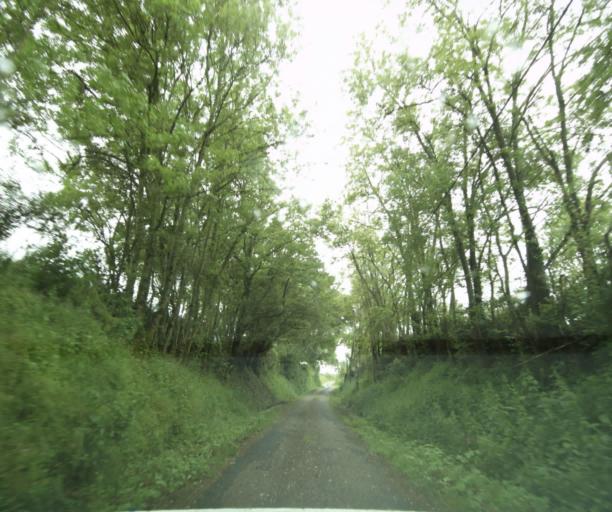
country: FR
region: Bourgogne
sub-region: Departement de Saone-et-Loire
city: Saint-Vallier
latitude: 46.4879
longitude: 4.4661
